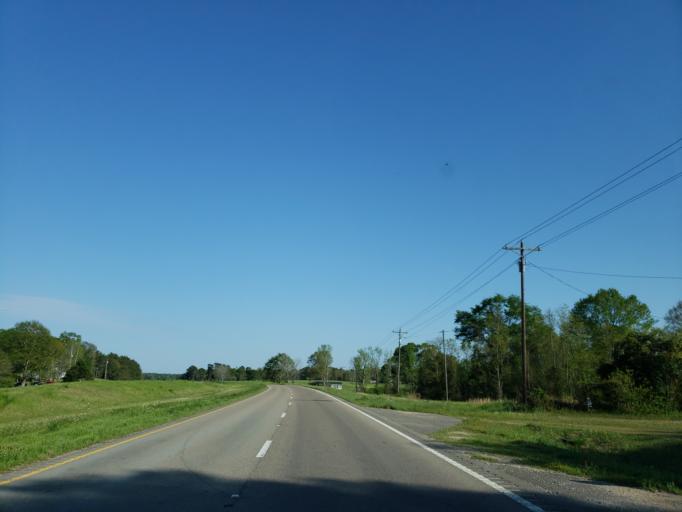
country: US
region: Mississippi
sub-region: Jones County
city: Ellisville
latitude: 31.6901
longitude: -89.3305
